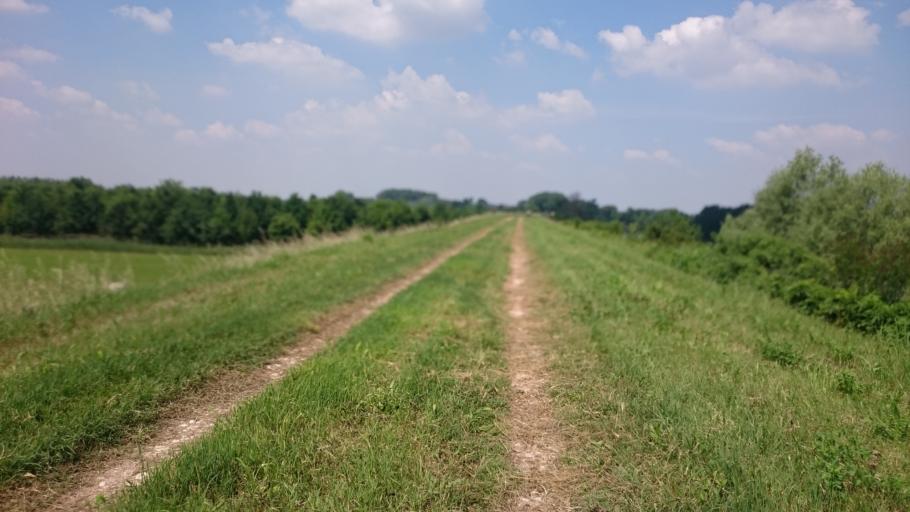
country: IT
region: Lombardy
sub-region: Provincia di Mantova
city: Bagnolo San Vito
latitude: 45.1063
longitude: 10.8814
